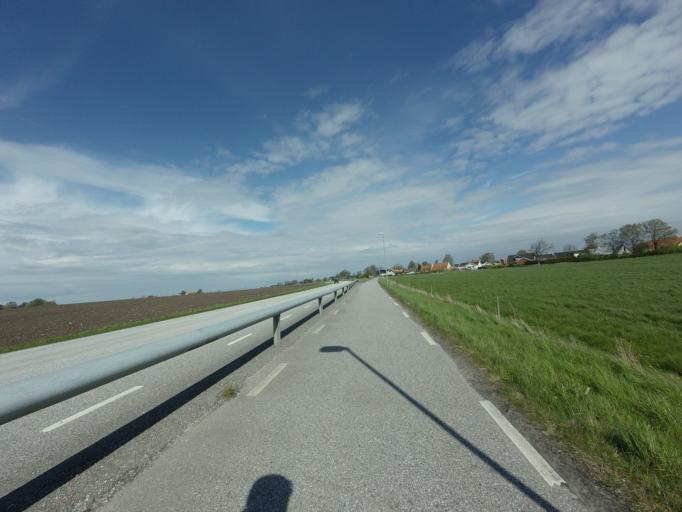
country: SE
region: Skane
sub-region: Vellinge Kommun
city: Vellinge
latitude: 55.4854
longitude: 13.0122
